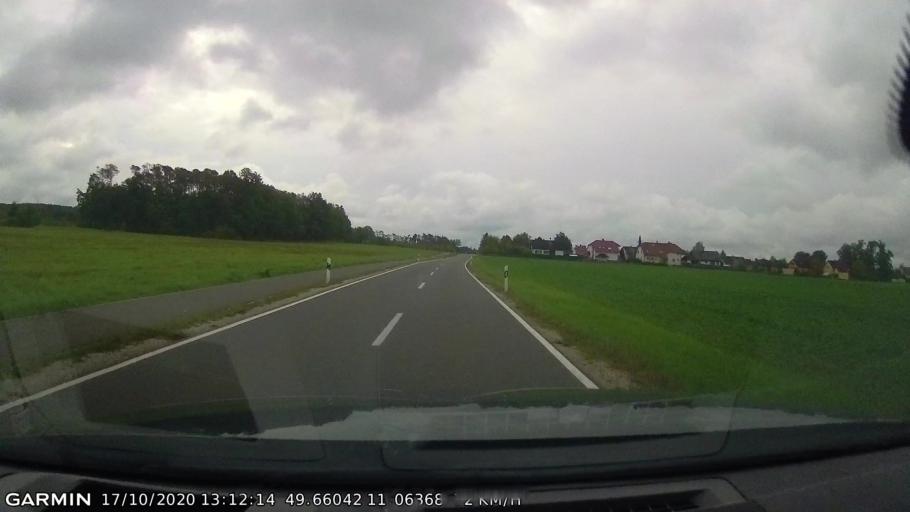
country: DE
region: Bavaria
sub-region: Upper Franconia
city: Poxdorf
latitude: 49.6601
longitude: 11.0637
